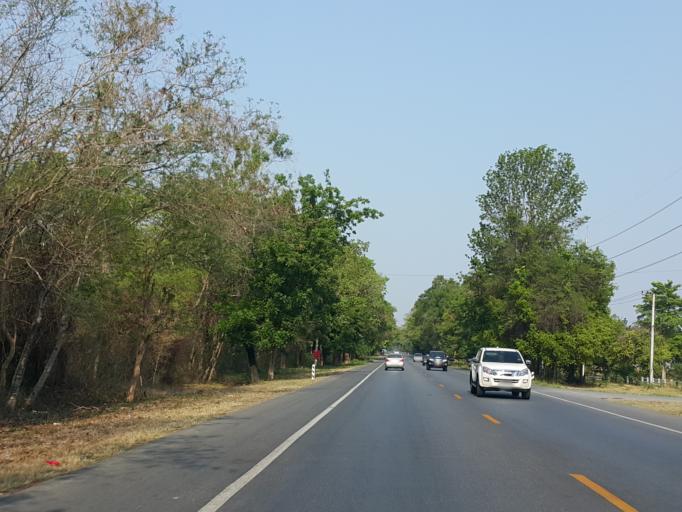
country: TH
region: Kanchanaburi
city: Sai Yok
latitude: 14.0899
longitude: 99.3050
